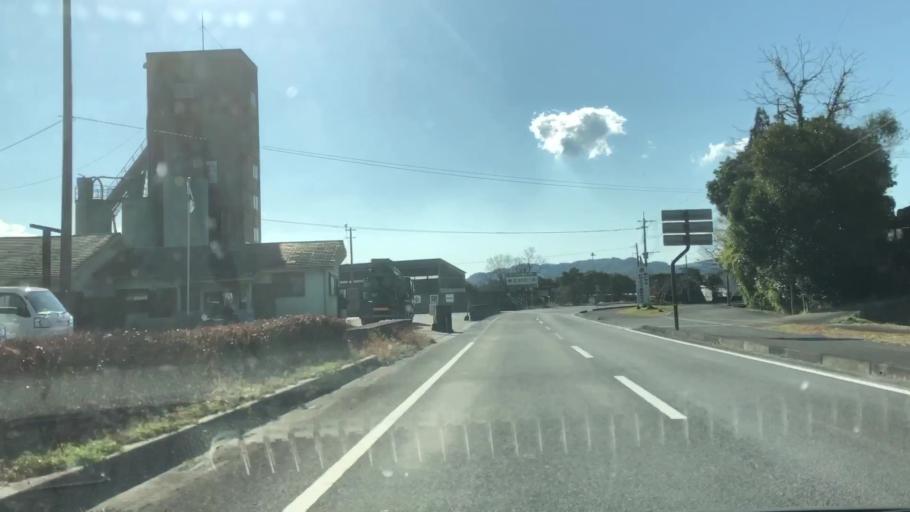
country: JP
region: Kagoshima
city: Satsumasendai
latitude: 31.8608
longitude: 130.4152
